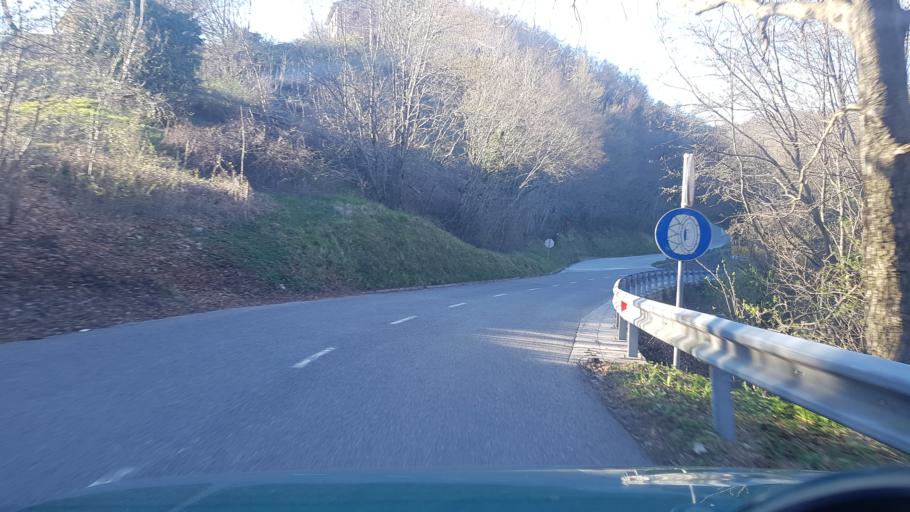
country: IT
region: Friuli Venezia Giulia
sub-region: Provincia di Gorizia
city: San Floriano del Collio
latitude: 46.0238
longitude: 13.5760
